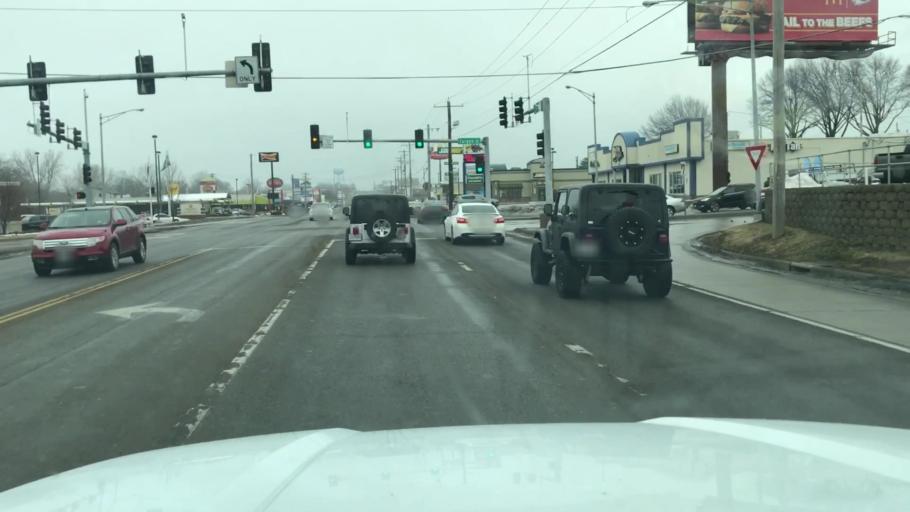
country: US
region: Missouri
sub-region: Buchanan County
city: Saint Joseph
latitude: 39.7693
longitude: -94.8035
